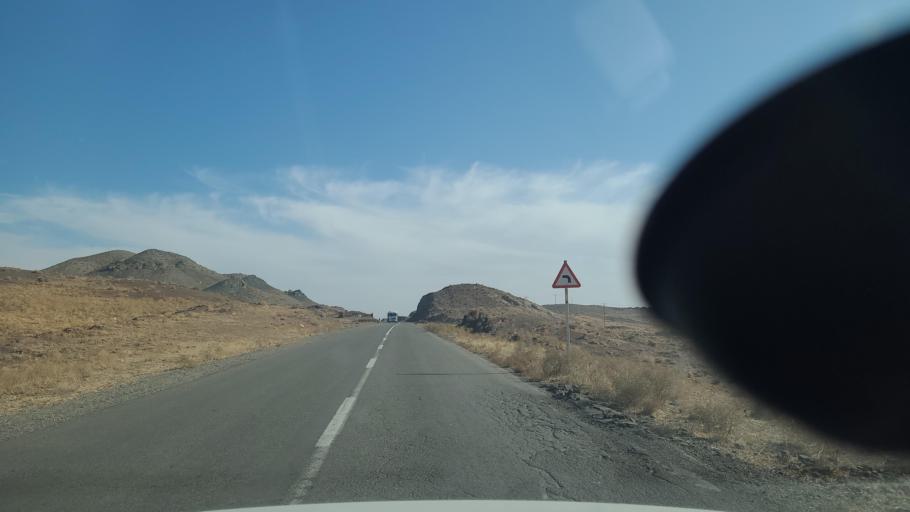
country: IR
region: Razavi Khorasan
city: Fariman
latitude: 35.5946
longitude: 59.7128
